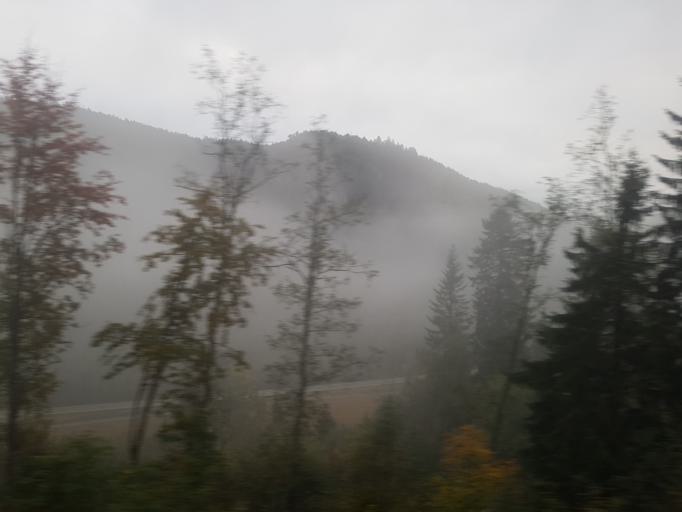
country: NO
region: Sor-Trondelag
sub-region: Midtre Gauldal
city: Storen
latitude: 62.9977
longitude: 10.2415
